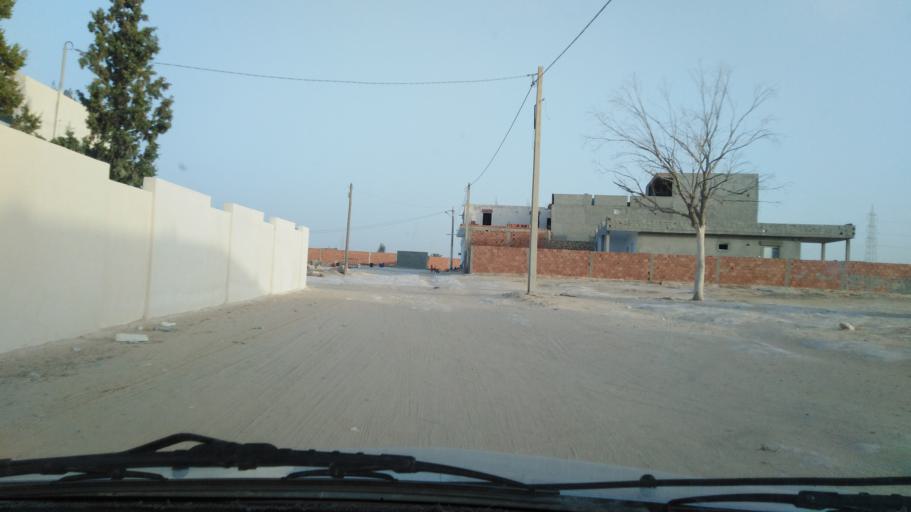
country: TN
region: Qabis
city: Gabes
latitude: 33.9524
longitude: 9.9958
